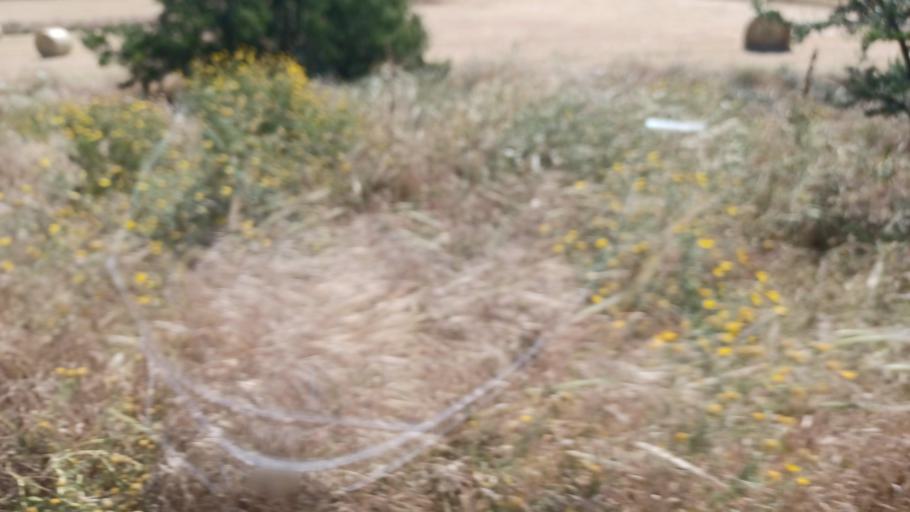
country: CY
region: Larnaka
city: Athienou
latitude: 34.9963
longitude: 33.5339
